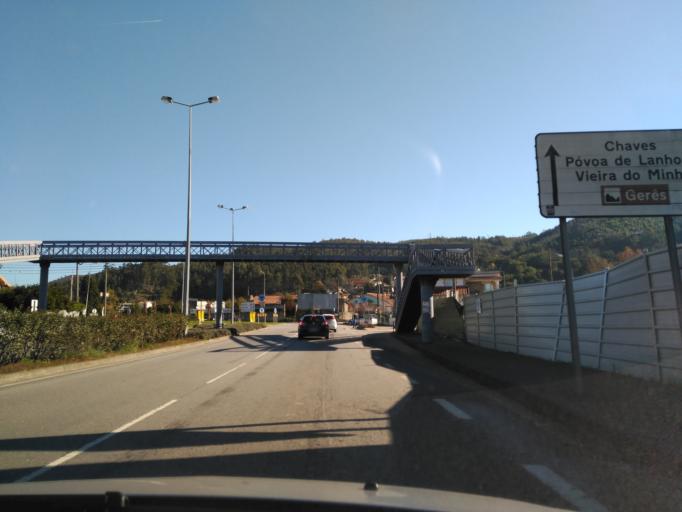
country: PT
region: Braga
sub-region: Braga
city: Adaufe
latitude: 41.5664
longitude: -8.3728
